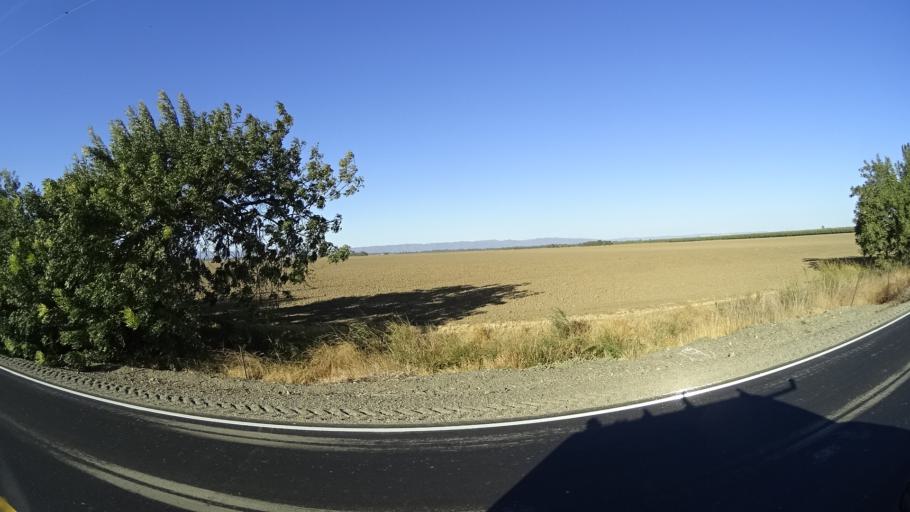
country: US
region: California
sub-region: Yolo County
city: Davis
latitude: 38.5716
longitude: -121.7860
